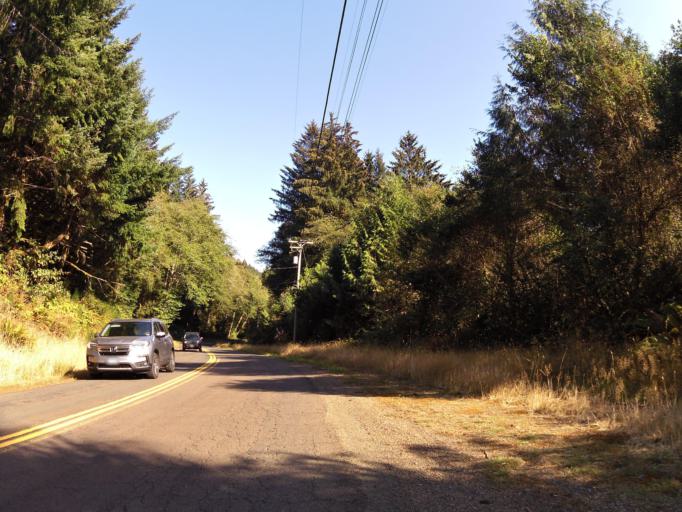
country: US
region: Oregon
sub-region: Lincoln County
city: Rose Lodge
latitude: 45.0801
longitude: -123.9435
